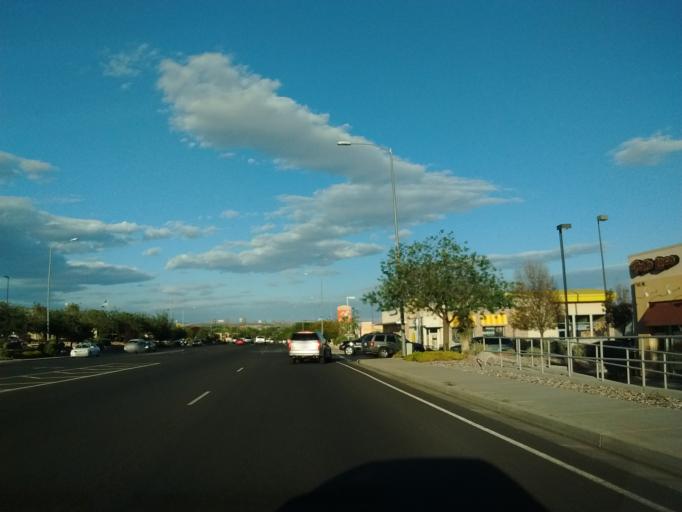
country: US
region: Utah
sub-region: Washington County
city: Washington
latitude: 37.1275
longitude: -113.5225
